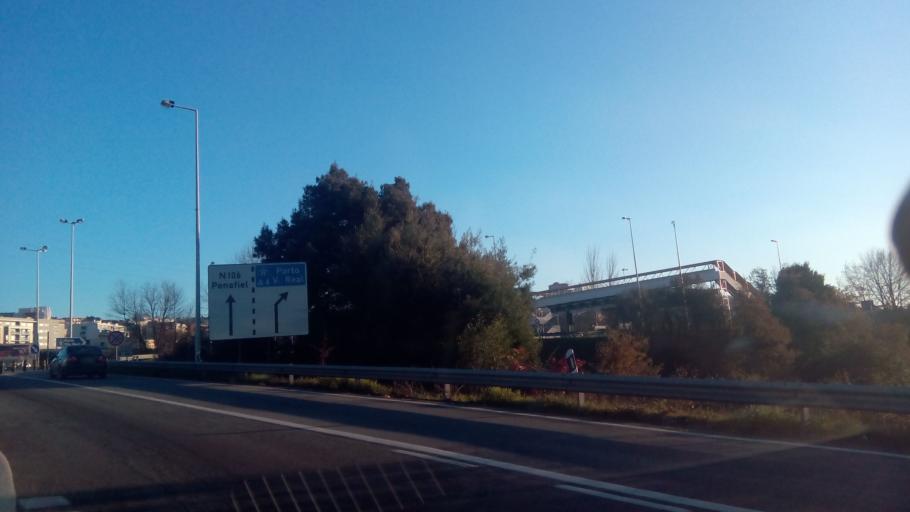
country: PT
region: Porto
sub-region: Penafiel
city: Penafiel
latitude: 41.2152
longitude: -8.2877
